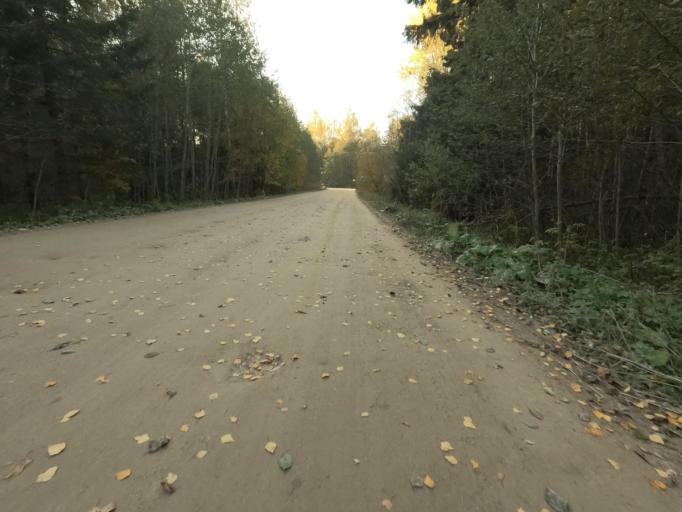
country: RU
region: Leningrad
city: Lyuban'
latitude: 59.0153
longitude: 31.0847
